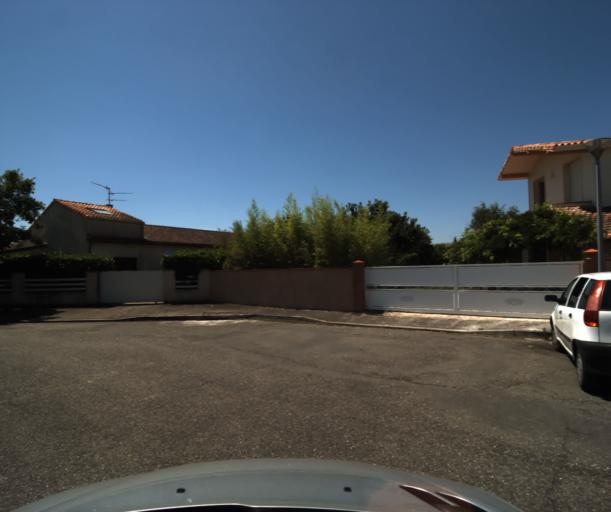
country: FR
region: Midi-Pyrenees
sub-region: Departement de la Haute-Garonne
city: Roquettes
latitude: 43.4975
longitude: 1.3795
